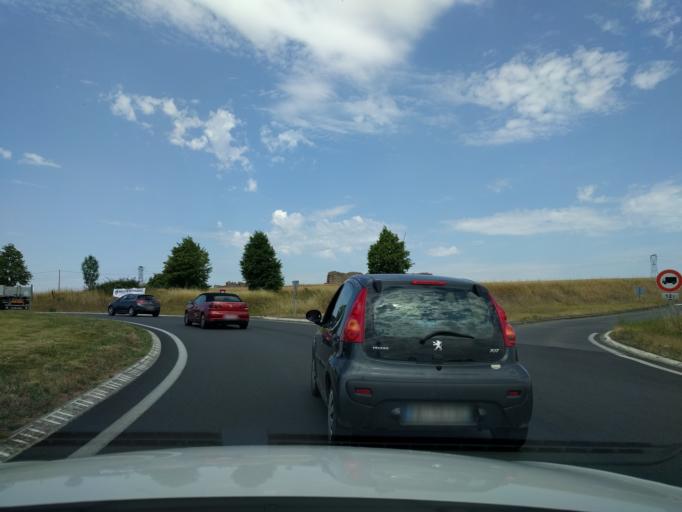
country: FR
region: Poitou-Charentes
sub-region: Departement des Deux-Sevres
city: Bessines
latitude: 46.3492
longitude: -0.5120
